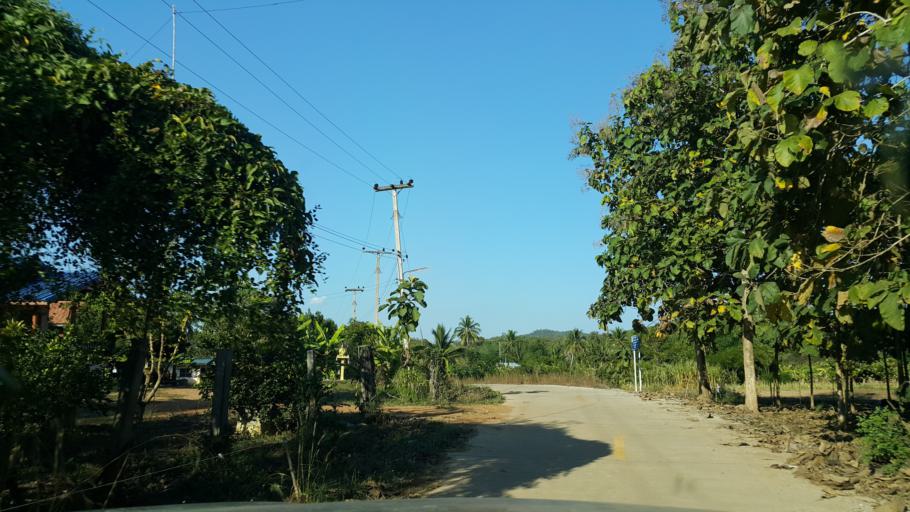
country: TH
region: Sukhothai
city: Thung Saliam
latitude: 17.3804
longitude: 99.5228
